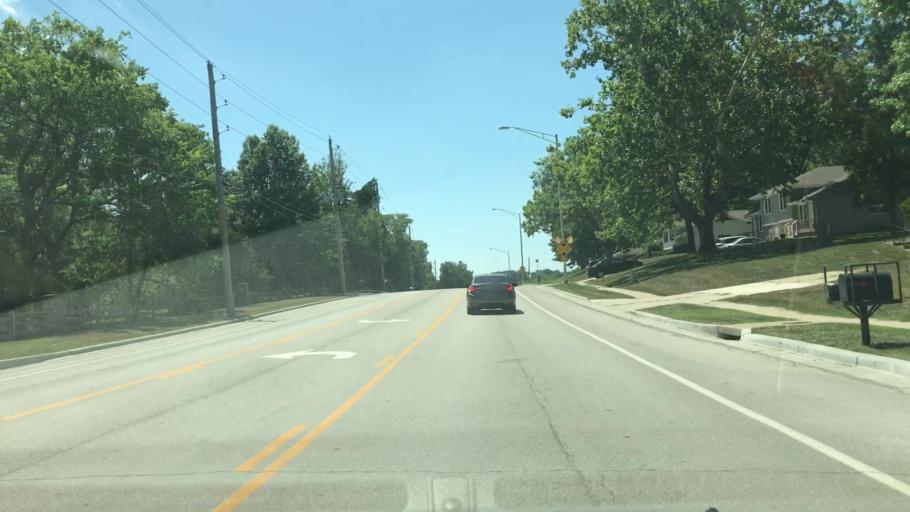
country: US
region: Missouri
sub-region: Jackson County
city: Lees Summit
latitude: 38.9273
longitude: -94.4308
